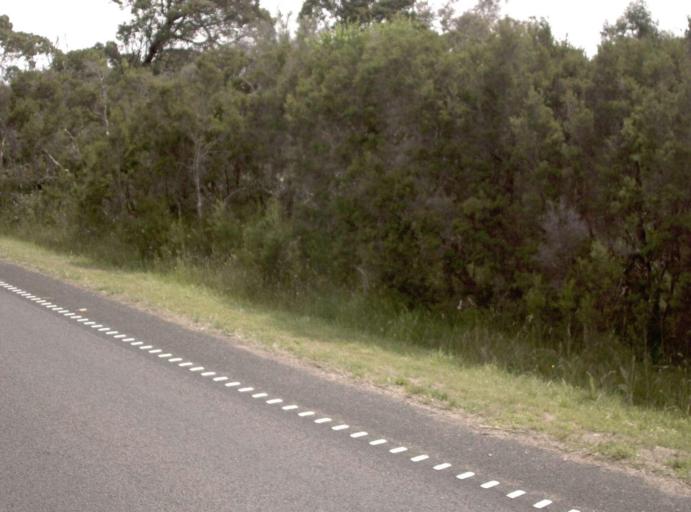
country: AU
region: Victoria
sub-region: Mornington Peninsula
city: Moorooduc
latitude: -38.2222
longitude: 145.1023
